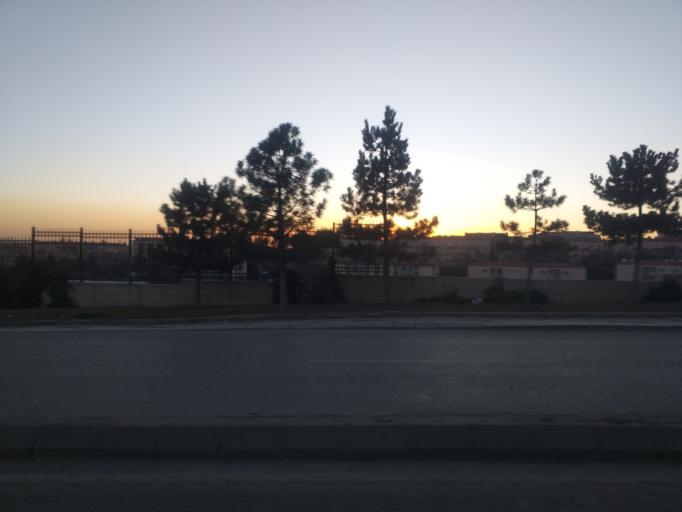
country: TR
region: Ankara
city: Ankara
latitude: 39.9618
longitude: 32.8219
